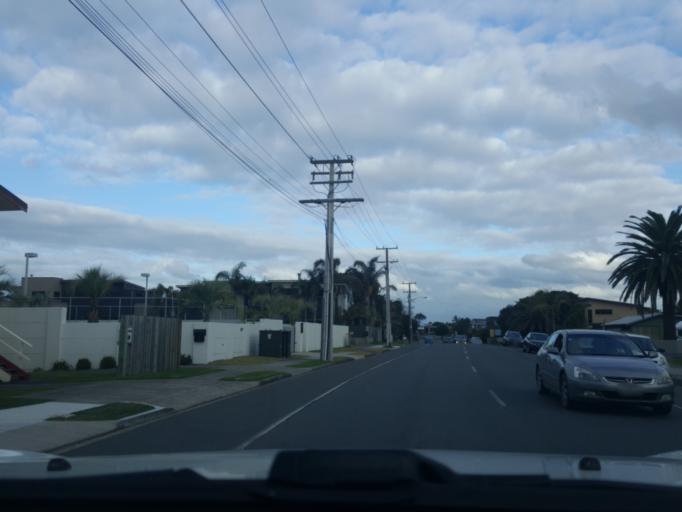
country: NZ
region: Bay of Plenty
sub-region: Tauranga City
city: Tauranga
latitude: -37.6561
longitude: 176.2099
